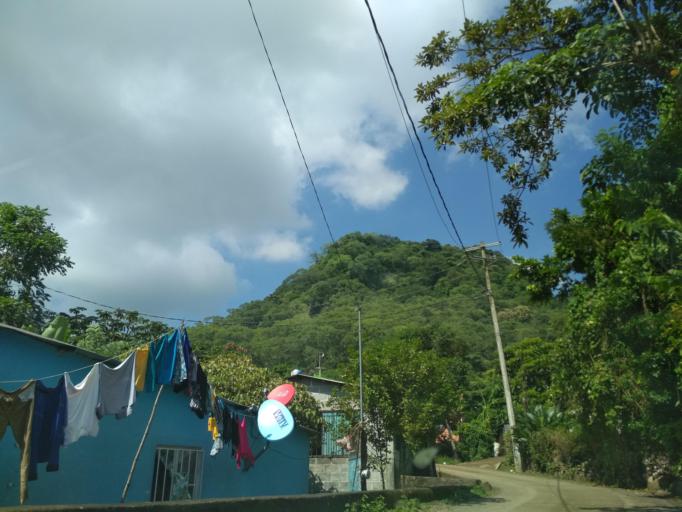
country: MX
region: Veracruz
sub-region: San Andres Tuxtla
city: Texcaltitan Xoteapan (Texcaltitan)
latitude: 18.4485
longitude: -95.2553
